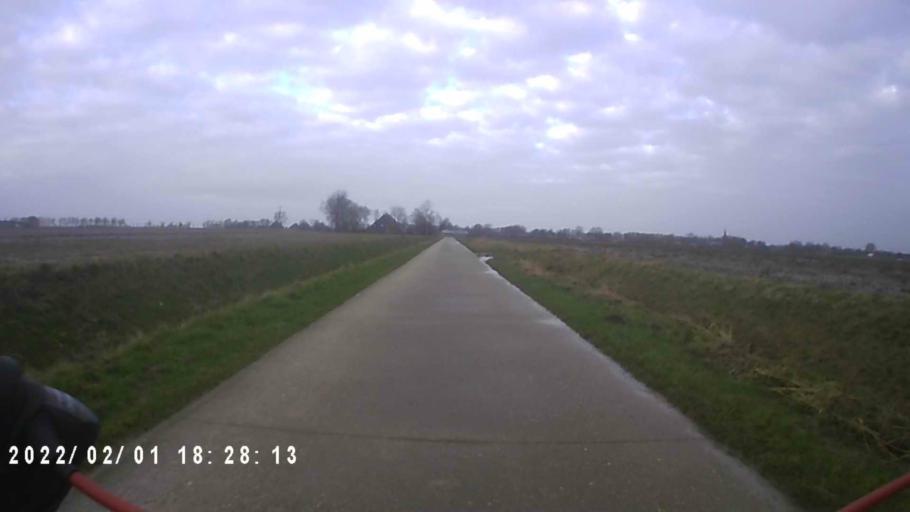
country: NL
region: Groningen
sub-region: Gemeente De Marne
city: Ulrum
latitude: 53.3510
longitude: 6.3192
